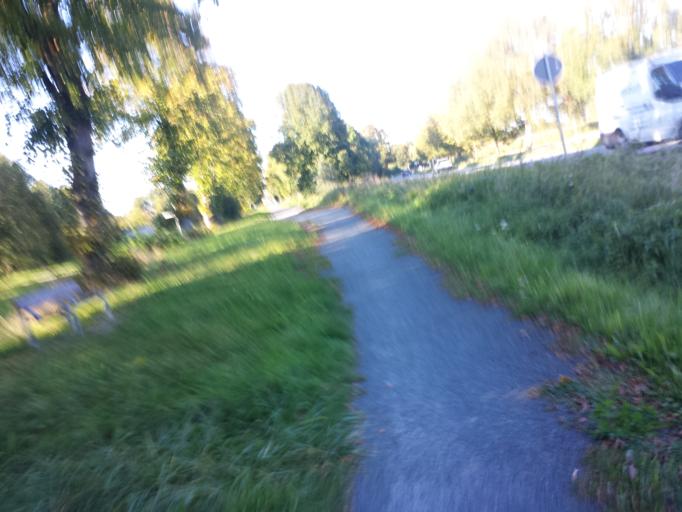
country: DE
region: North Rhine-Westphalia
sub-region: Regierungsbezirk Detmold
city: Langenberg
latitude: 51.7694
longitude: 8.3243
